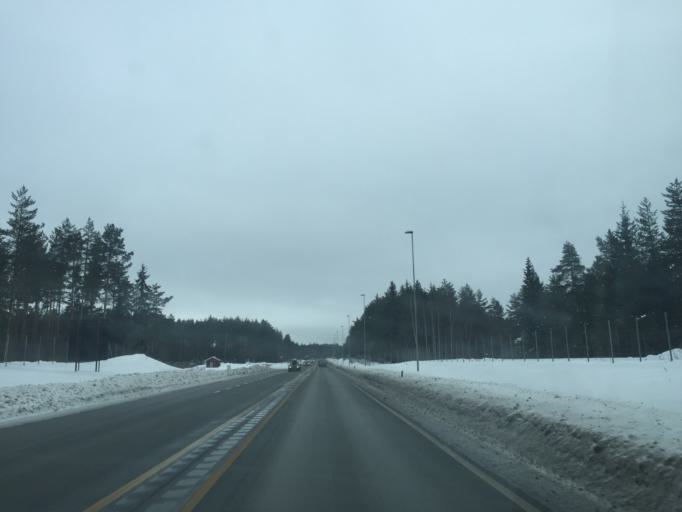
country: NO
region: Hedmark
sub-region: Stange
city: Stange
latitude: 60.7084
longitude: 11.2791
